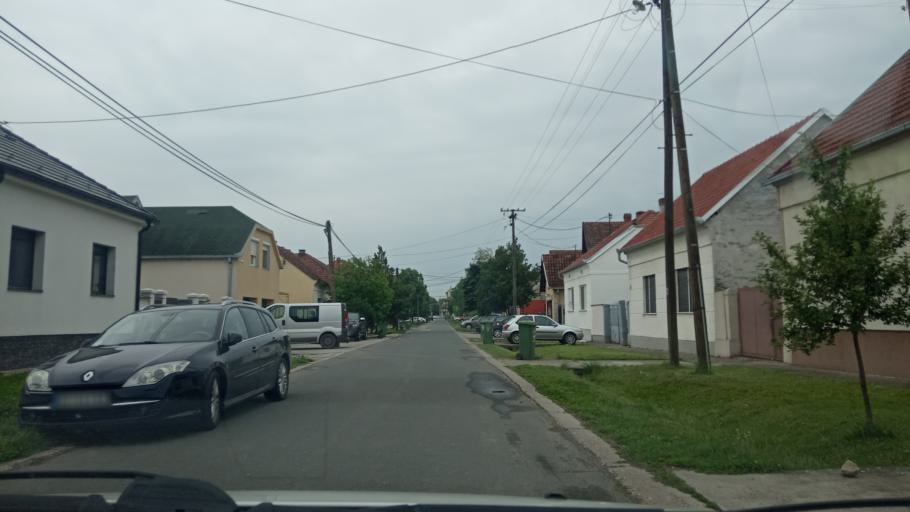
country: RS
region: Autonomna Pokrajina Vojvodina
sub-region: Sremski Okrug
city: Stara Pazova
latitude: 44.9890
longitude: 20.1540
